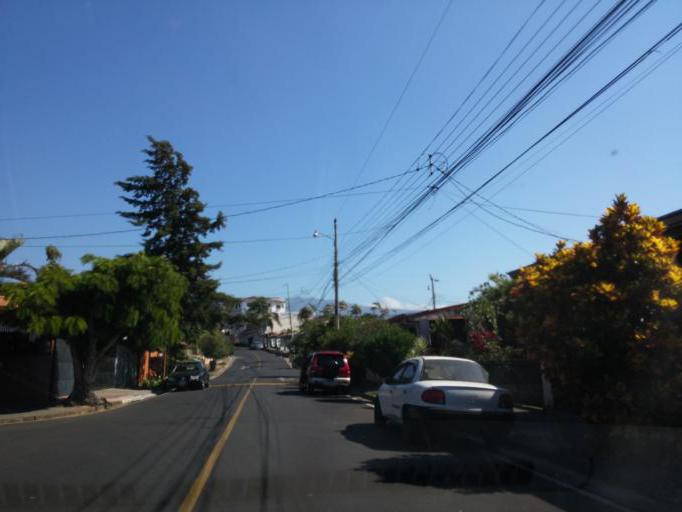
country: CR
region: Alajuela
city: Alajuela
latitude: 10.0132
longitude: -84.2054
